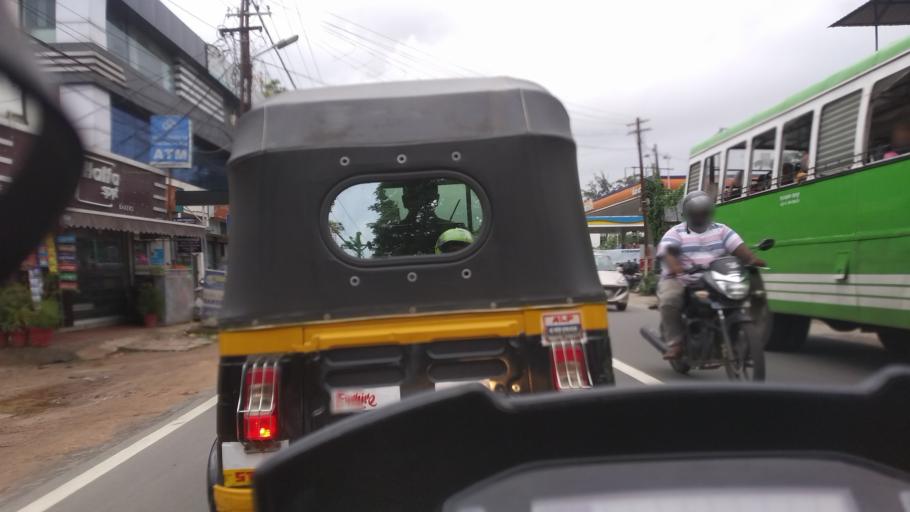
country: IN
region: Kerala
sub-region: Alappuzha
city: Alleppey
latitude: 9.4895
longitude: 76.3384
